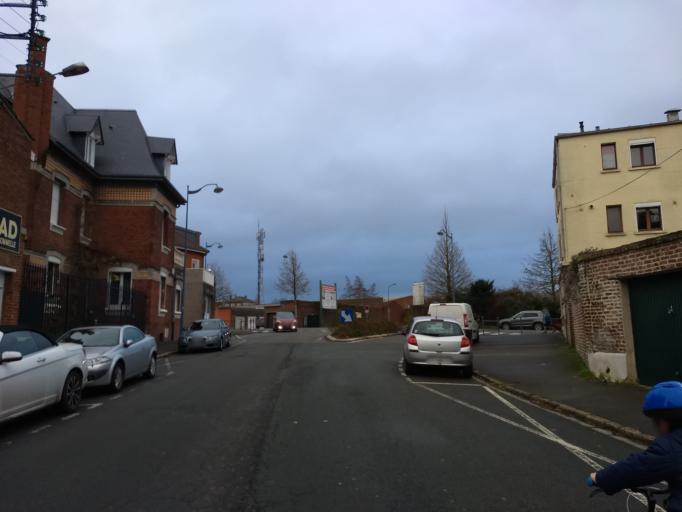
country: FR
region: Nord-Pas-de-Calais
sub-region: Departement du Pas-de-Calais
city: Arras
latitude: 50.2848
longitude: 2.7725
